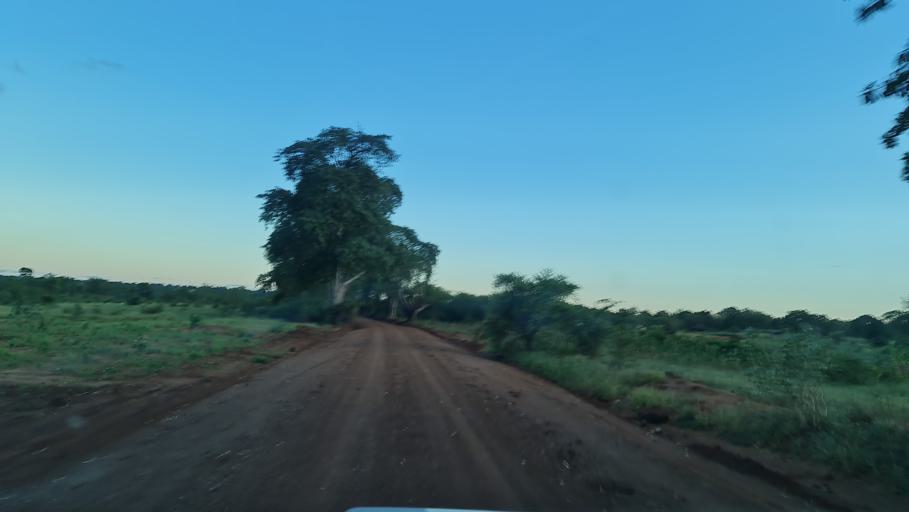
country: MZ
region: Nampula
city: Ilha de Mocambique
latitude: -14.9768
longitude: 40.0925
